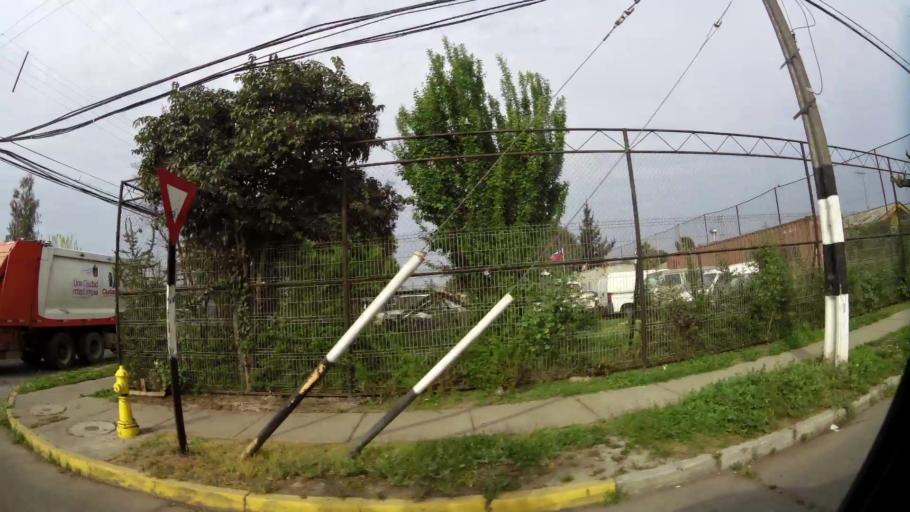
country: CL
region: Santiago Metropolitan
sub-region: Provincia de Santiago
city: Lo Prado
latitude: -33.5196
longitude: -70.7666
